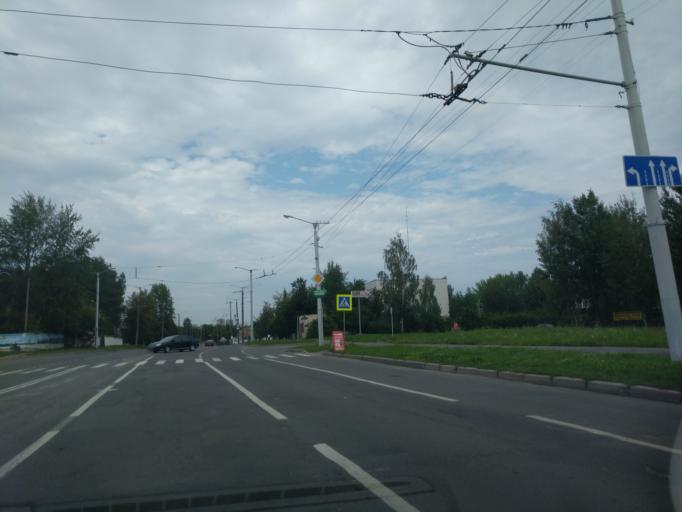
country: BY
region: Minsk
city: Novoye Medvezhino
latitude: 53.8847
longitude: 27.4814
